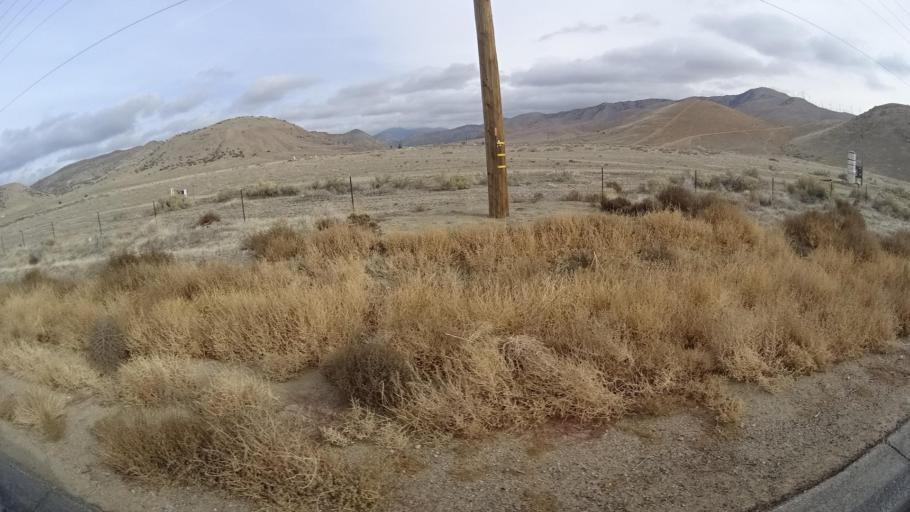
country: US
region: California
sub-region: Kern County
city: Tehachapi
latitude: 35.1143
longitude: -118.3329
